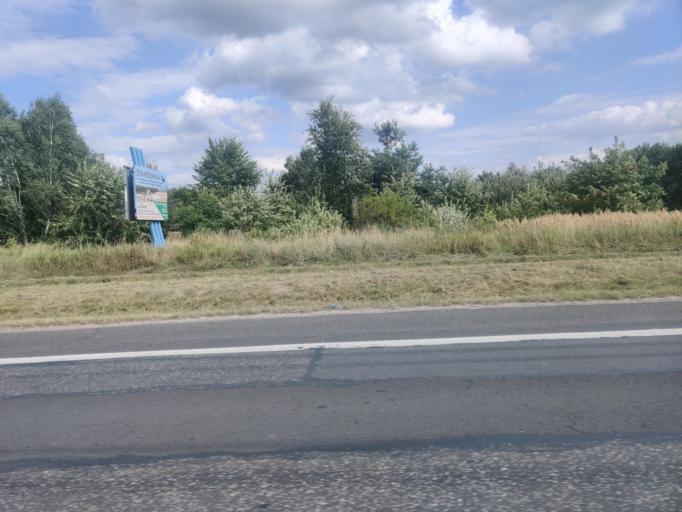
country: PL
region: Greater Poland Voivodeship
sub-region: Konin
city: Konin
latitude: 52.1975
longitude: 18.2685
